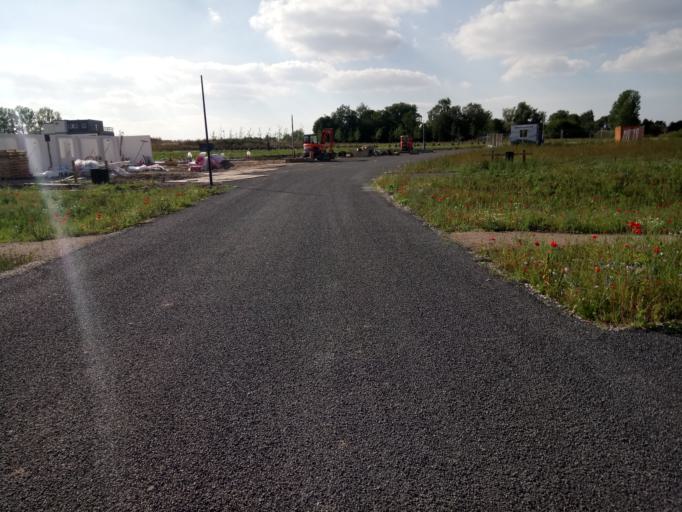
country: DK
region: Capital Region
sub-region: Egedal Kommune
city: Olstykke
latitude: 55.8128
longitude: 12.1213
